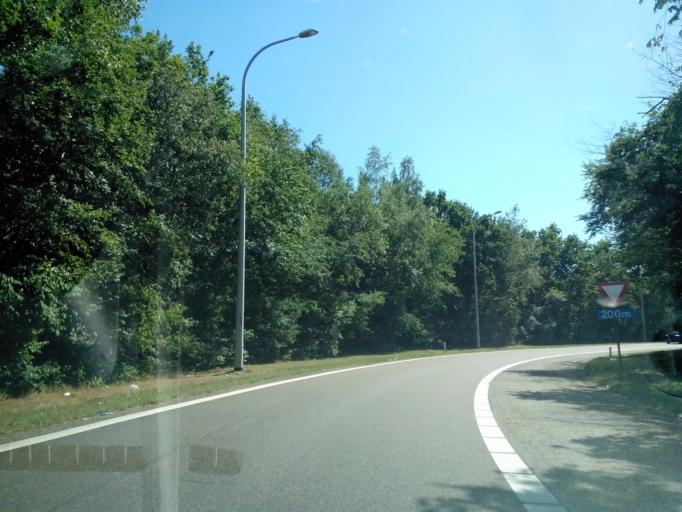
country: BE
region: Flanders
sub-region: Provincie Limburg
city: Genk
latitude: 50.9911
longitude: 5.5030
